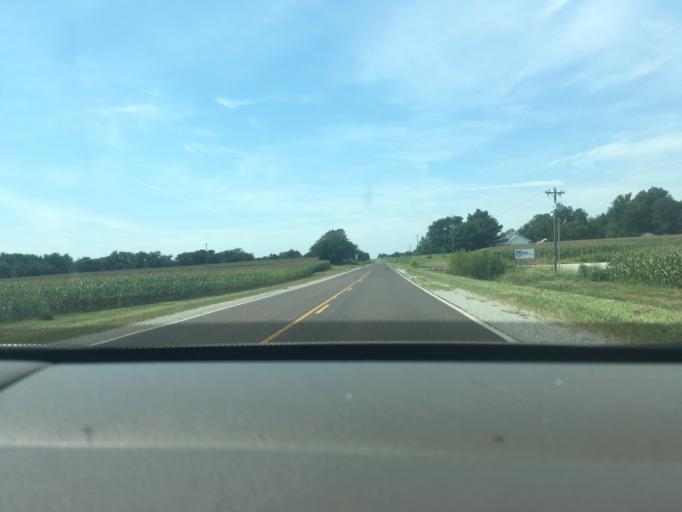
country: US
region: Missouri
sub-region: Nodaway County
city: Maryville
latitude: 40.1712
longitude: -94.8333
